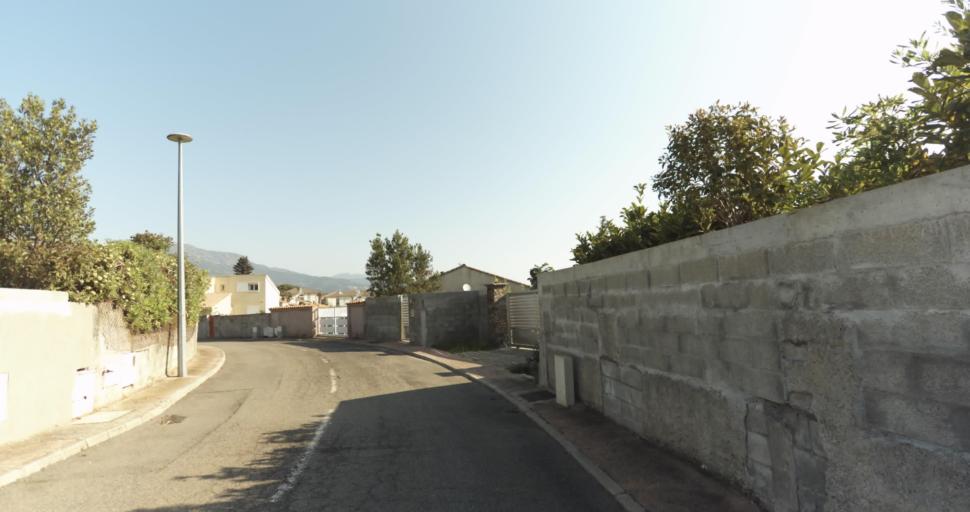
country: FR
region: Corsica
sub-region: Departement de la Haute-Corse
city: Biguglia
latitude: 42.6373
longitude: 9.4320
